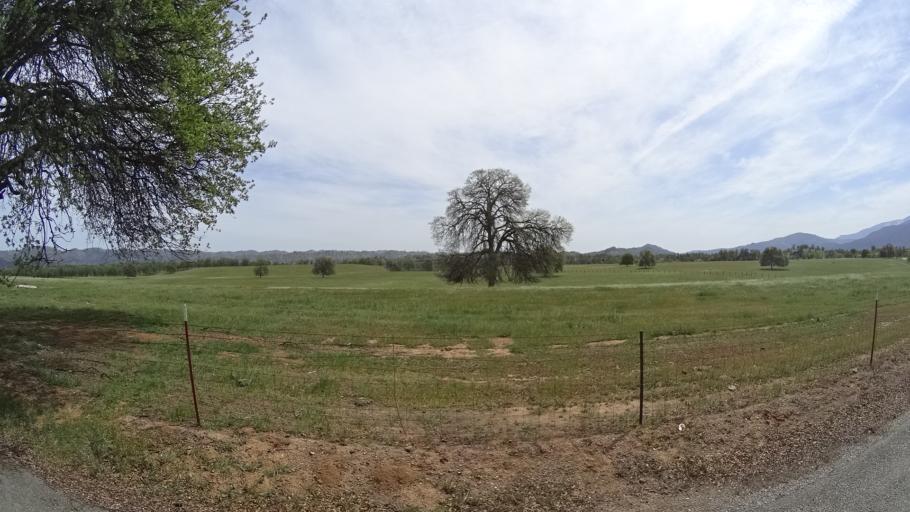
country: US
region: California
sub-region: Glenn County
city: Willows
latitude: 39.5900
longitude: -122.5749
